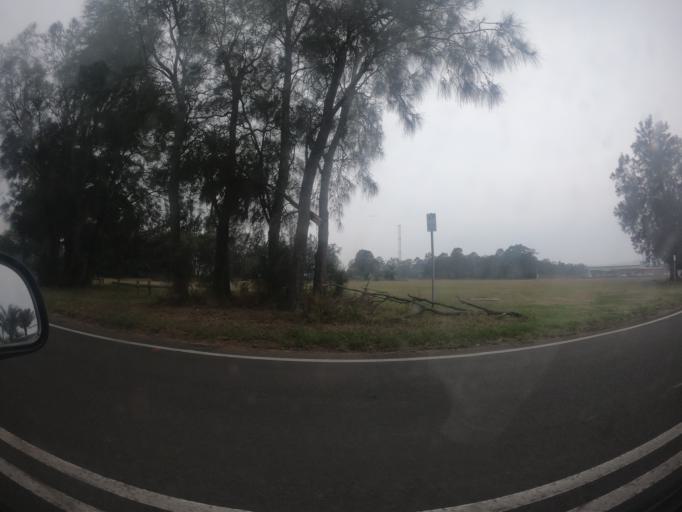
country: AU
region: New South Wales
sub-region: Shellharbour
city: Albion Park Rail
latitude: -34.5576
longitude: 150.7901
